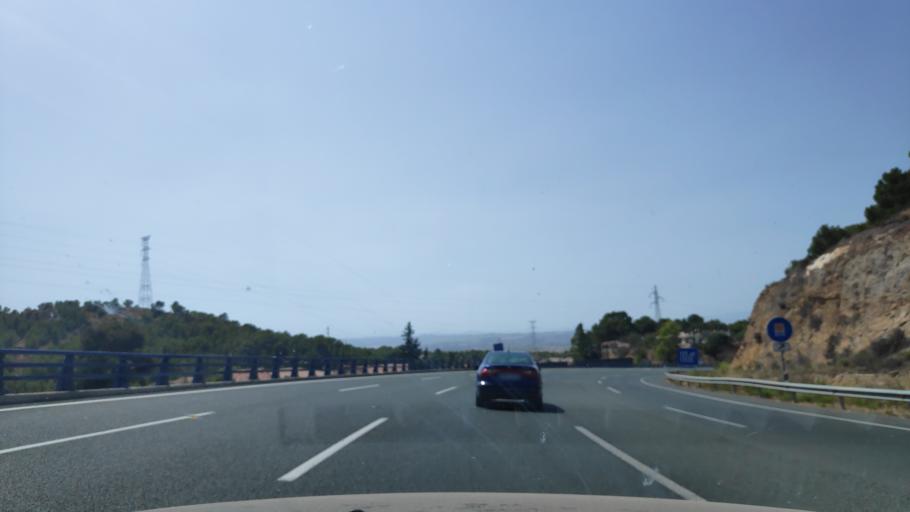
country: ES
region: Murcia
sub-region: Murcia
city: Alcantarilla
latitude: 37.9090
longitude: -1.1615
